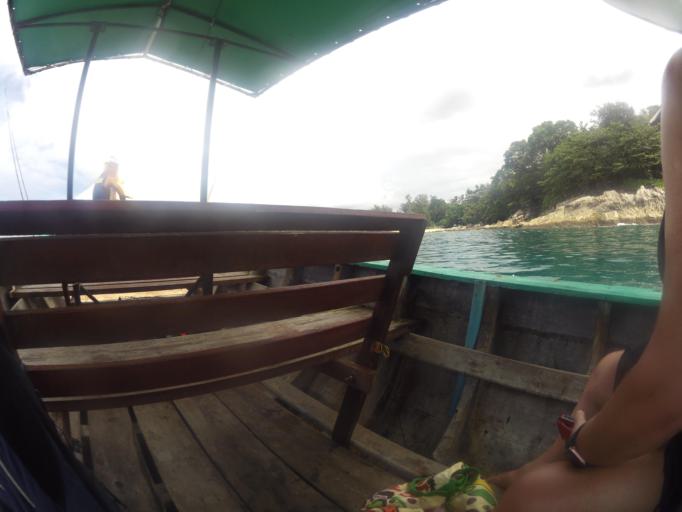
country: TH
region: Phuket
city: Patong
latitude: 7.9684
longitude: 98.2762
